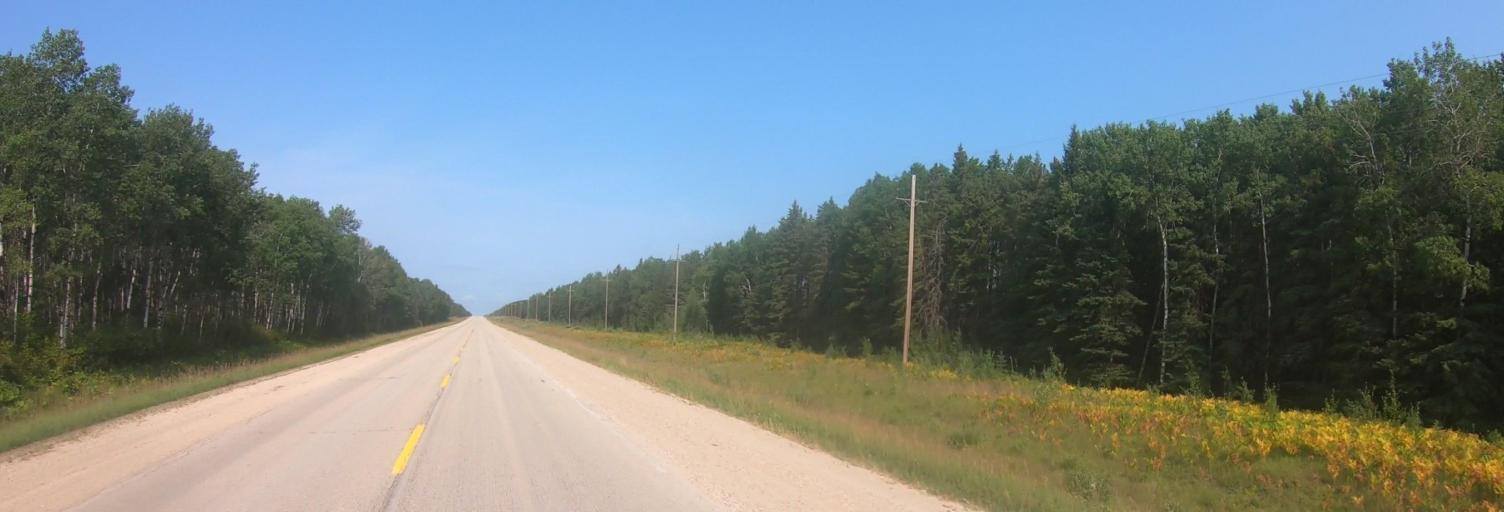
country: US
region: Minnesota
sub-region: Roseau County
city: Roseau
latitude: 49.1179
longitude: -96.0495
